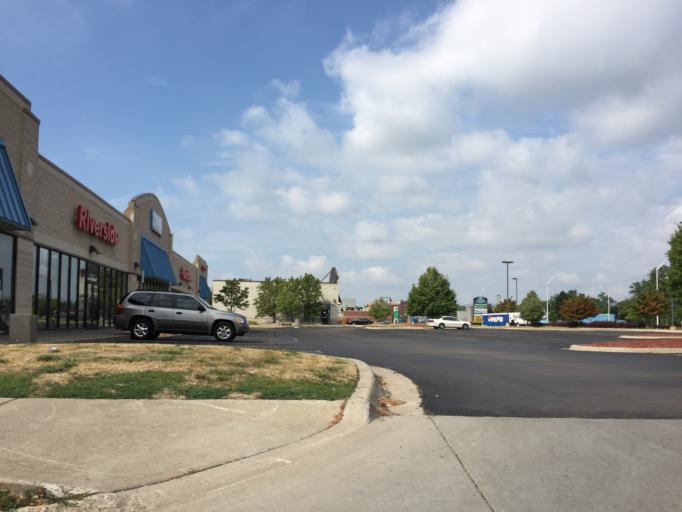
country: US
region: Michigan
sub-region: Wayne County
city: Grosse Pointe Park
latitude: 42.3653
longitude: -82.9725
